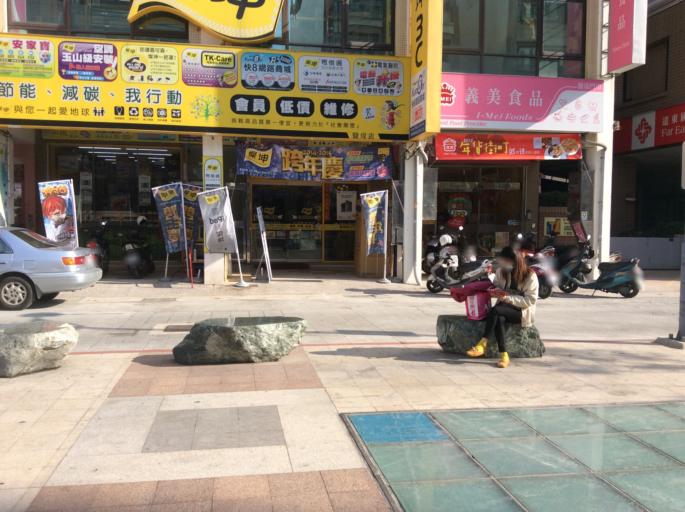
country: TW
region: Kaohsiung
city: Kaohsiung
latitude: 22.6252
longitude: 120.2847
